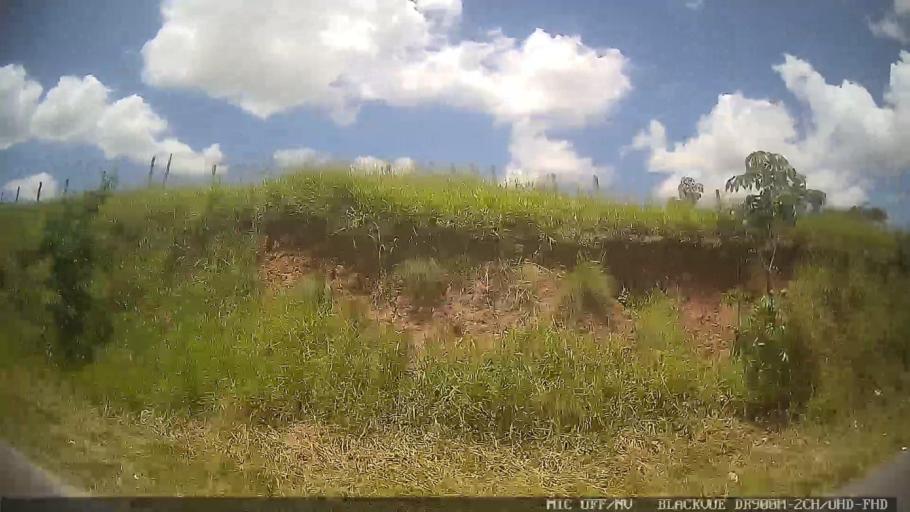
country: BR
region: Sao Paulo
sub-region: Jacarei
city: Jacarei
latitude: -23.3105
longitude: -45.9358
